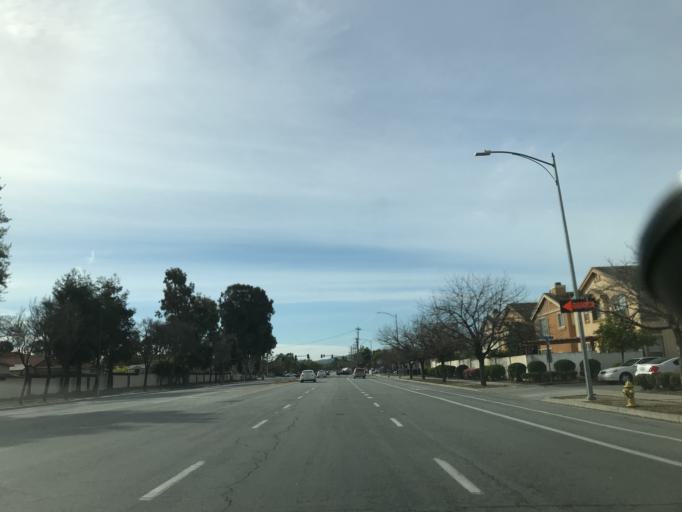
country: US
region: California
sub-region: Santa Clara County
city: Alum Rock
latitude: 37.3268
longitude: -121.7977
